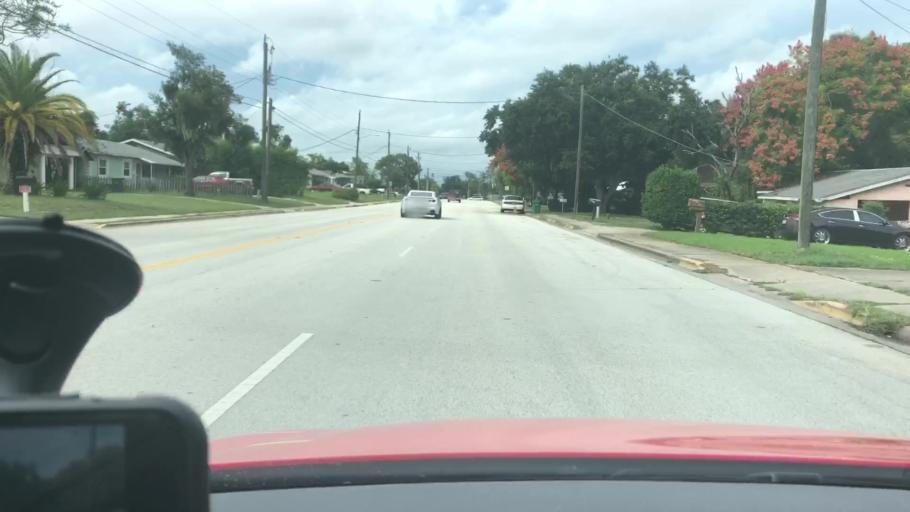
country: US
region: Florida
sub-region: Volusia County
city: Daytona Beach
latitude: 29.2149
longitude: -81.0529
